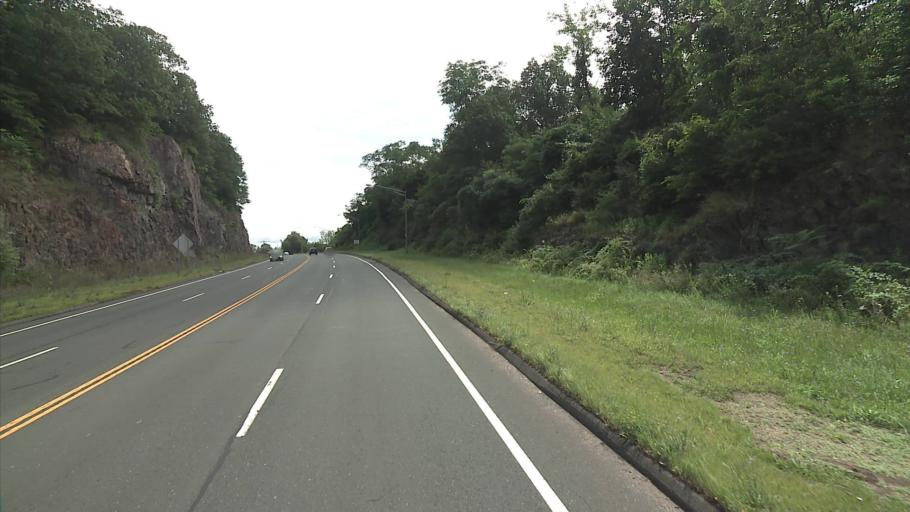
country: US
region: Connecticut
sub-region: Hartford County
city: Newington
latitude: 41.6983
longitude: -72.7115
